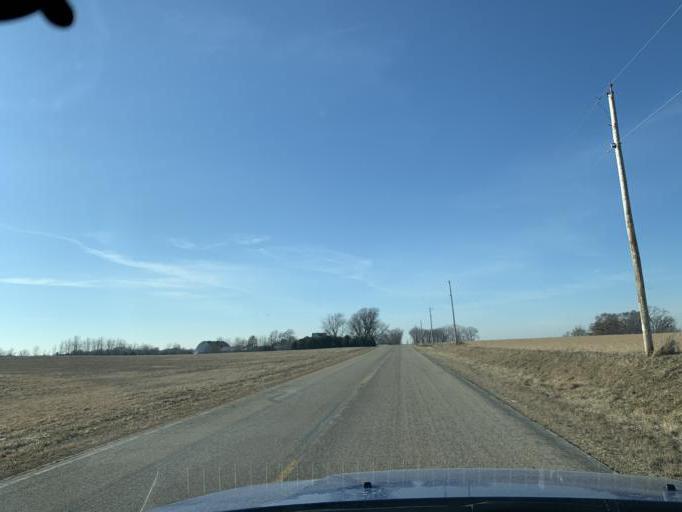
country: US
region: Wisconsin
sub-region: Iowa County
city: Barneveld
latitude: 42.8207
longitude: -89.9237
